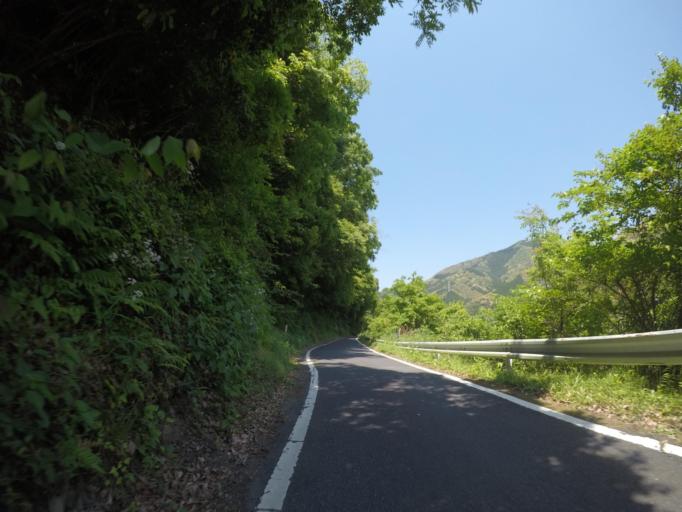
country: JP
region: Shizuoka
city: Shizuoka-shi
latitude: 35.0131
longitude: 138.2691
